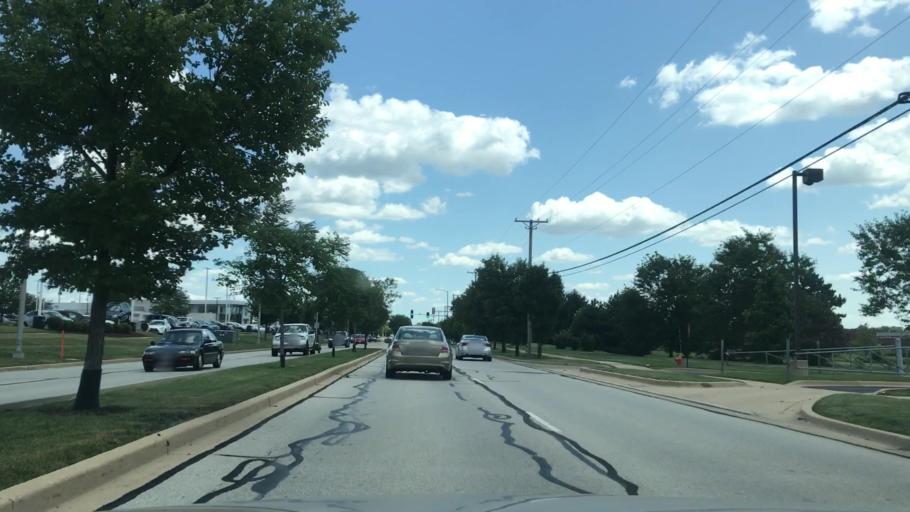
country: US
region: Illinois
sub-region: DuPage County
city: Naperville
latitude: 41.7636
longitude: -88.1933
